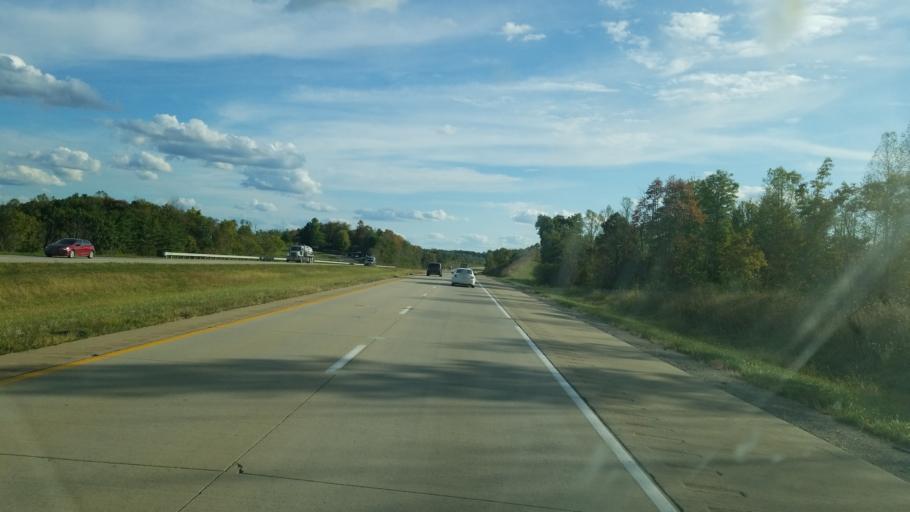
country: US
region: Ohio
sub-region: Washington County
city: Devola
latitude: 39.5576
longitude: -81.4486
